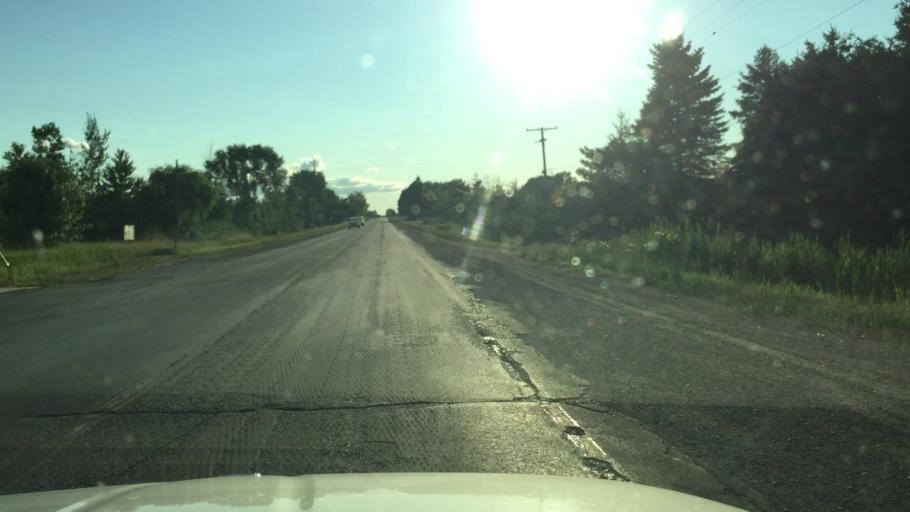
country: US
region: Michigan
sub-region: Lapeer County
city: Imlay City
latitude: 43.0251
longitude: -83.0084
